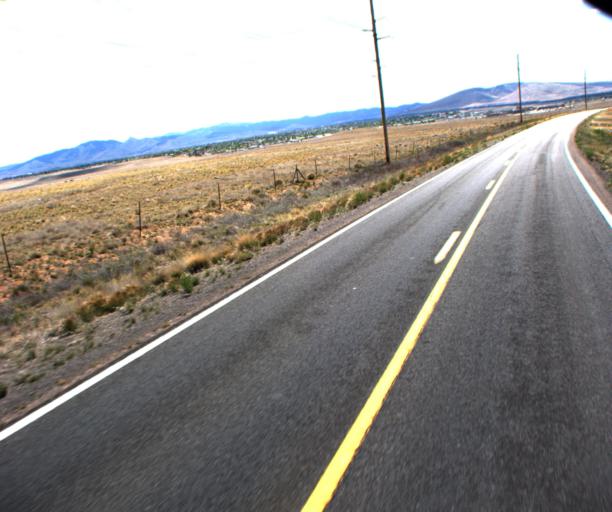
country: US
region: Arizona
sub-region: Yavapai County
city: Prescott Valley
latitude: 34.6446
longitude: -112.2977
